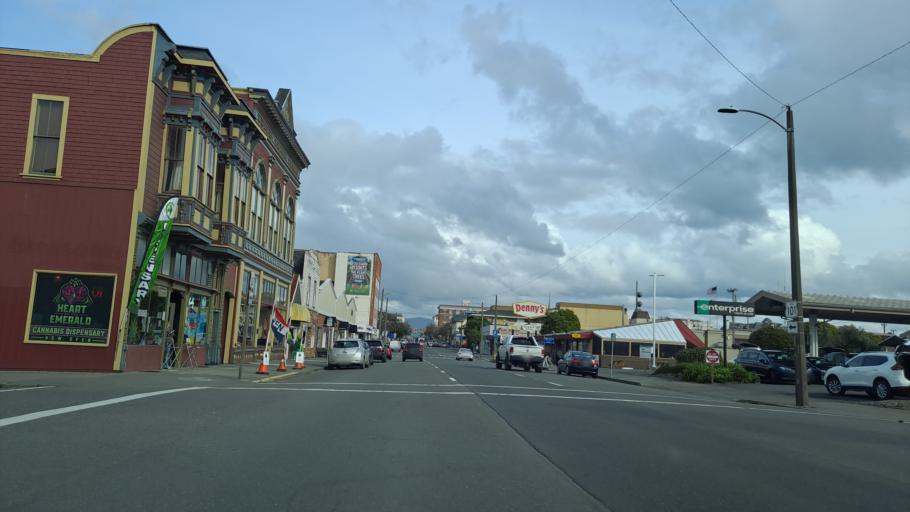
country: US
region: California
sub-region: Humboldt County
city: Eureka
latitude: 40.8013
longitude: -124.1704
